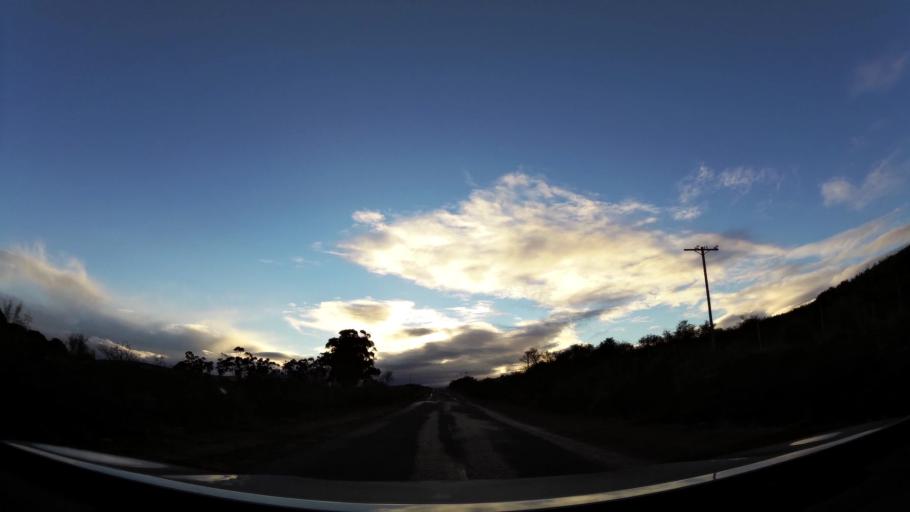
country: ZA
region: Western Cape
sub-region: Eden District Municipality
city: Riversdale
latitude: -34.0648
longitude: 20.8902
